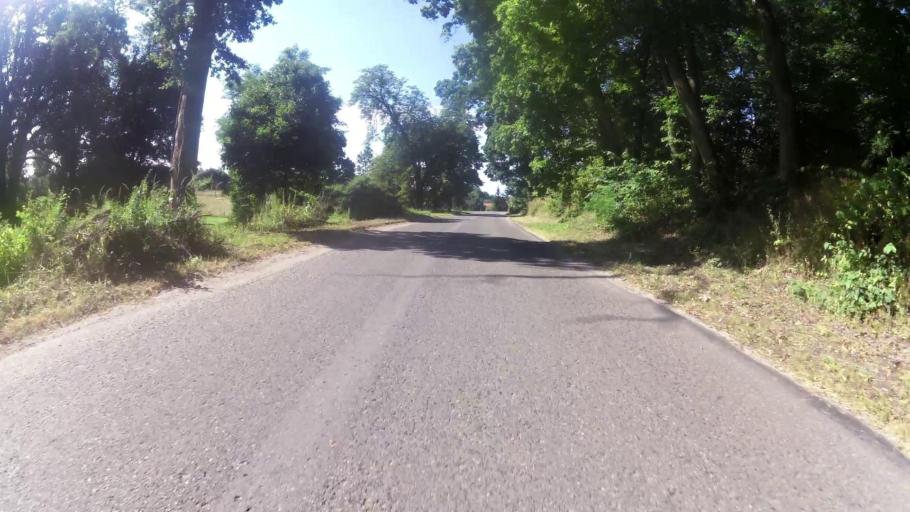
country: PL
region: West Pomeranian Voivodeship
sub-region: Powiat stargardzki
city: Insko
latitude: 53.4464
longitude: 15.6446
